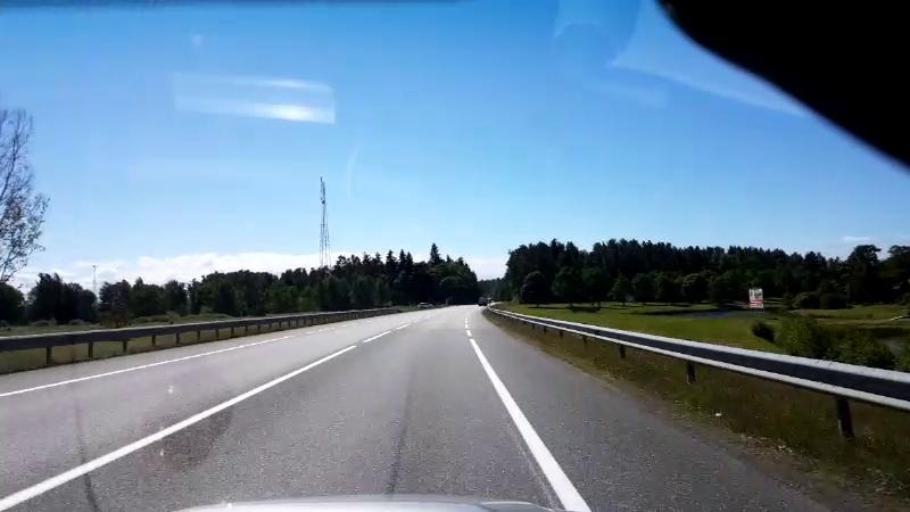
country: LV
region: Saulkrastu
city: Saulkrasti
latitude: 57.4045
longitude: 24.4307
